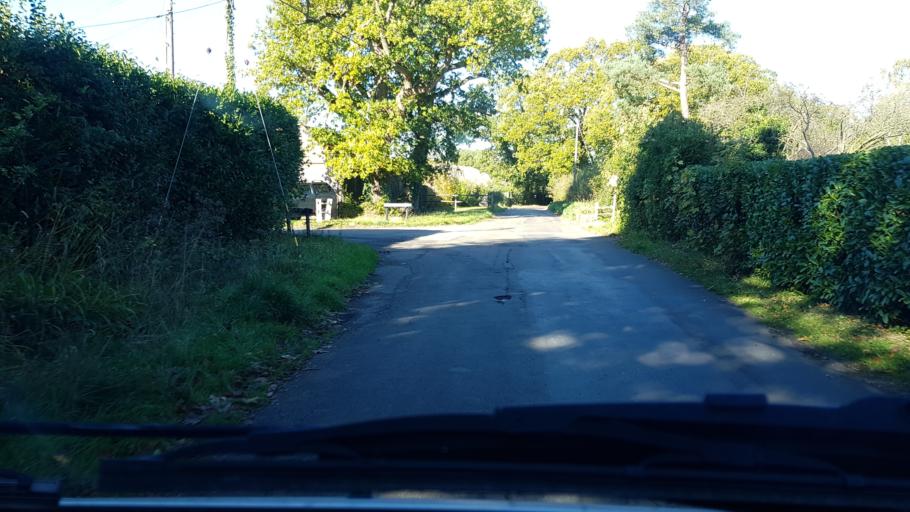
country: GB
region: England
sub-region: Surrey
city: Ockley
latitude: 51.1434
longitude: -0.3350
